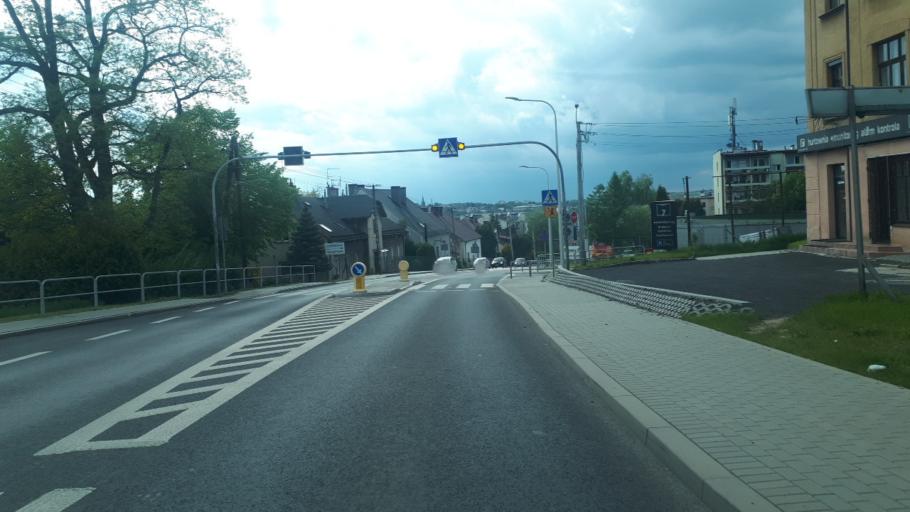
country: PL
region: Silesian Voivodeship
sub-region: Bielsko-Biala
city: Bielsko-Biala
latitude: 49.8208
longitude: 19.0645
